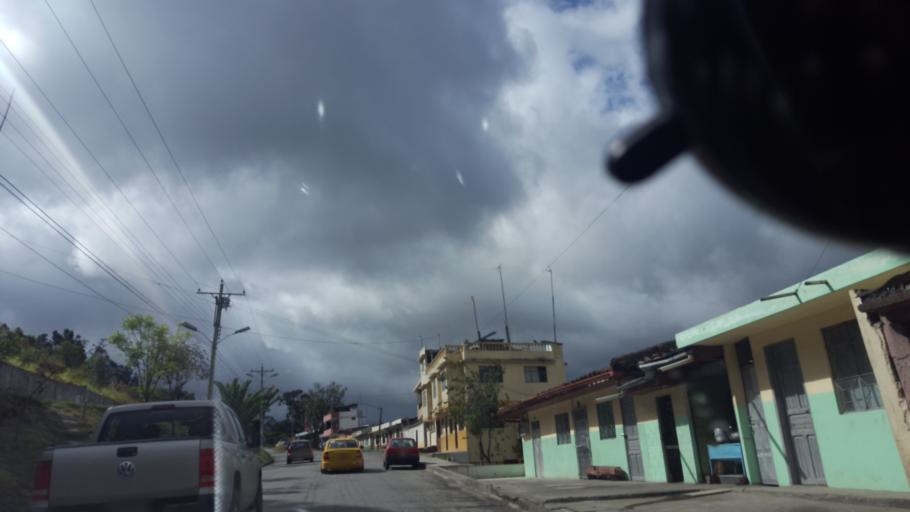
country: EC
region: Loja
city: Loja
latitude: -4.0002
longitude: -79.2078
